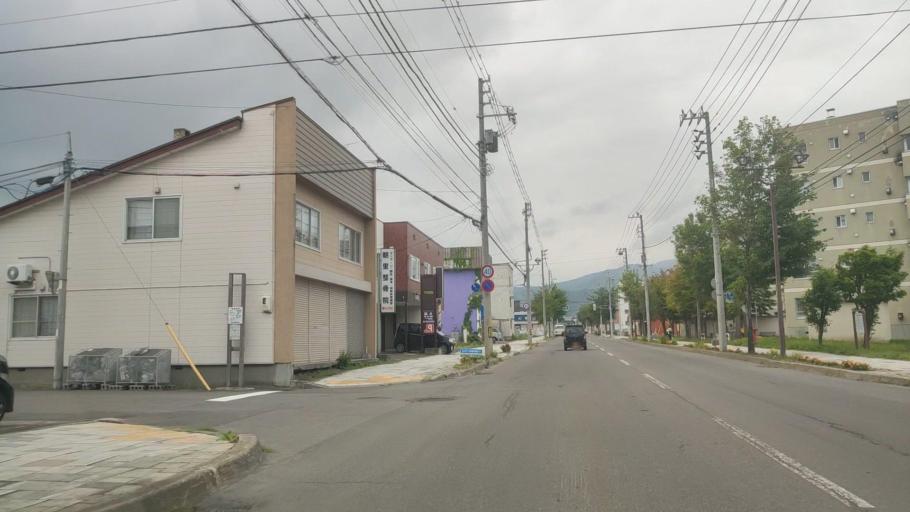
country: JP
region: Hokkaido
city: Otaru
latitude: 43.1727
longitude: 141.0551
